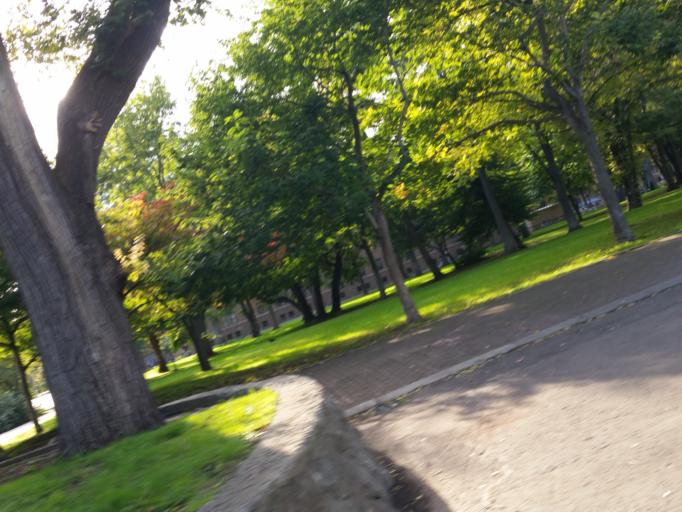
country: JP
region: Hokkaido
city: Sapporo
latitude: 43.0699
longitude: 141.3434
